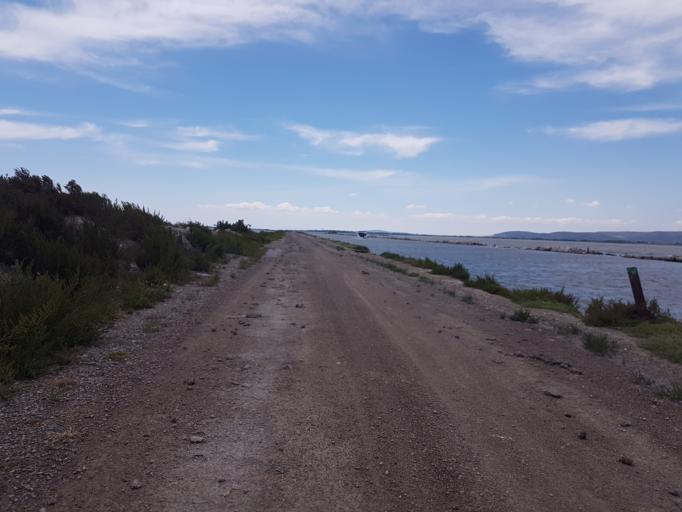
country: FR
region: Languedoc-Roussillon
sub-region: Departement de l'Herault
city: Villeneuve-les-Maguelone
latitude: 43.4953
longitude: 3.8525
